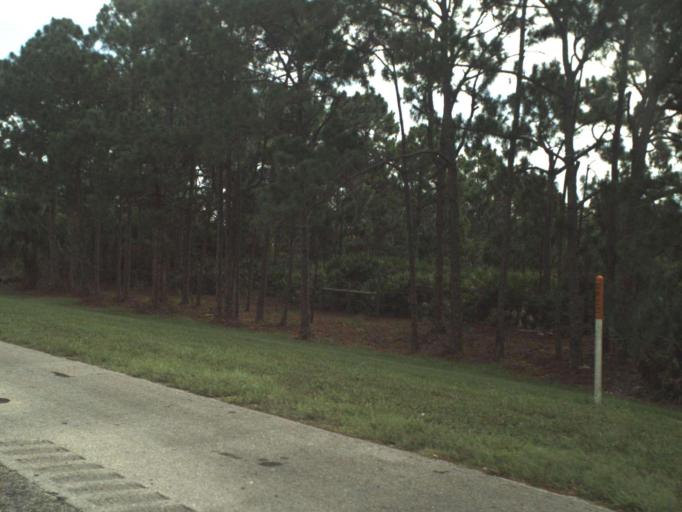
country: US
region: Florida
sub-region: Saint Lucie County
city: River Park
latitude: 27.3278
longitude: -80.4132
